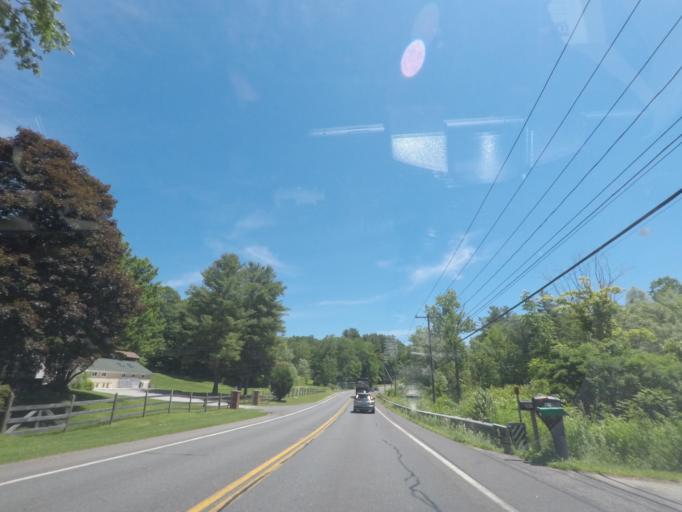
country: US
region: Massachusetts
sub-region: Berkshire County
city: Lee
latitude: 42.2948
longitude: -73.1700
